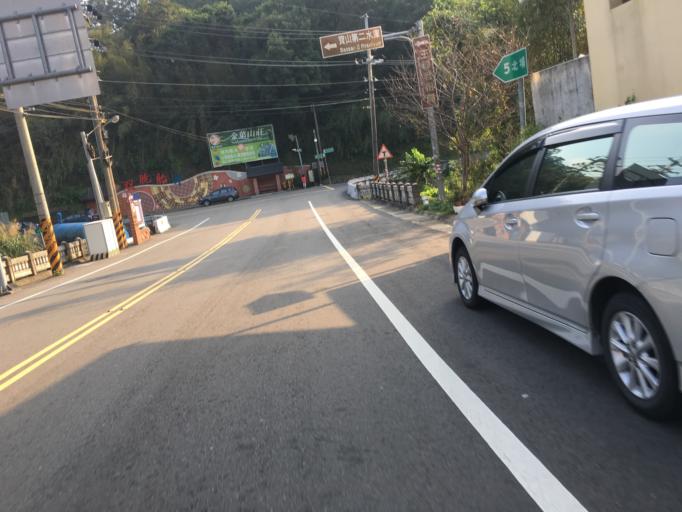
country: TW
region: Taiwan
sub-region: Hsinchu
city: Hsinchu
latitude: 24.7333
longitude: 121.0276
